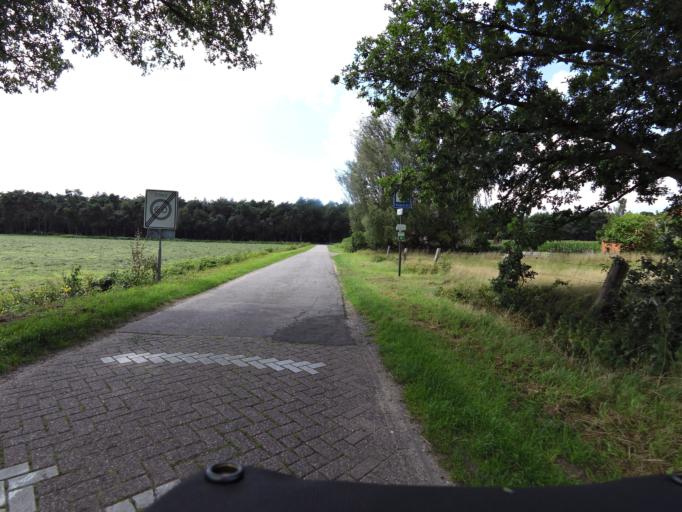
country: BE
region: Flanders
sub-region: Provincie Antwerpen
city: Baarle-Hertog
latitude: 51.4321
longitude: 4.8260
